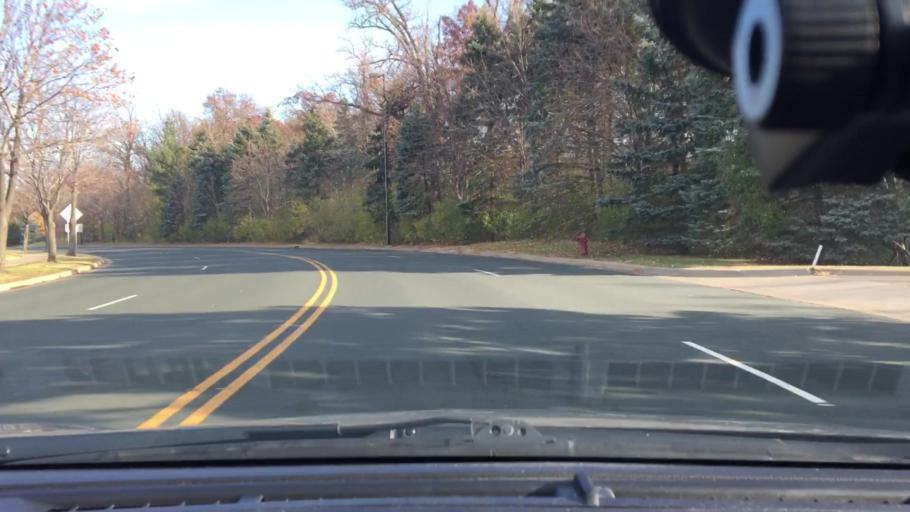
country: US
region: Minnesota
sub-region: Hennepin County
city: Maple Grove
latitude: 45.0716
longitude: -93.4419
